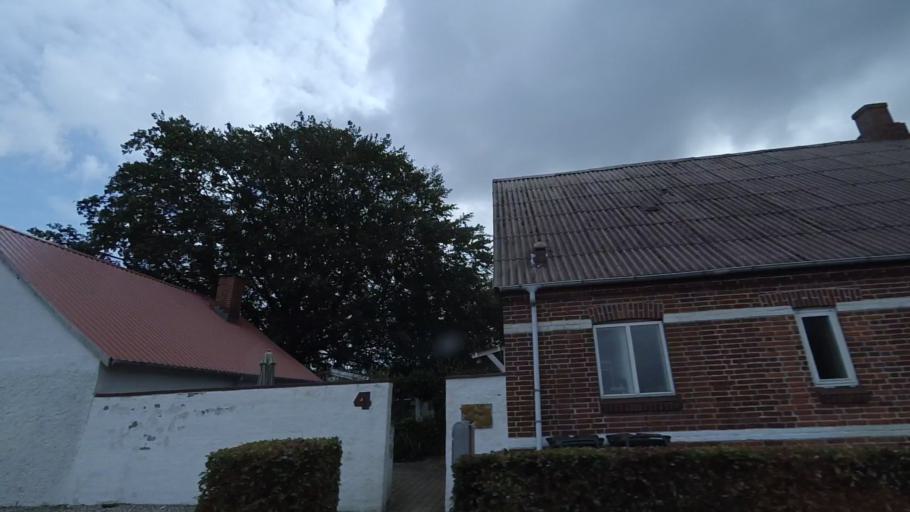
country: DK
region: Central Jutland
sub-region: Syddjurs Kommune
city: Ryomgard
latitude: 56.3961
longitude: 10.5513
